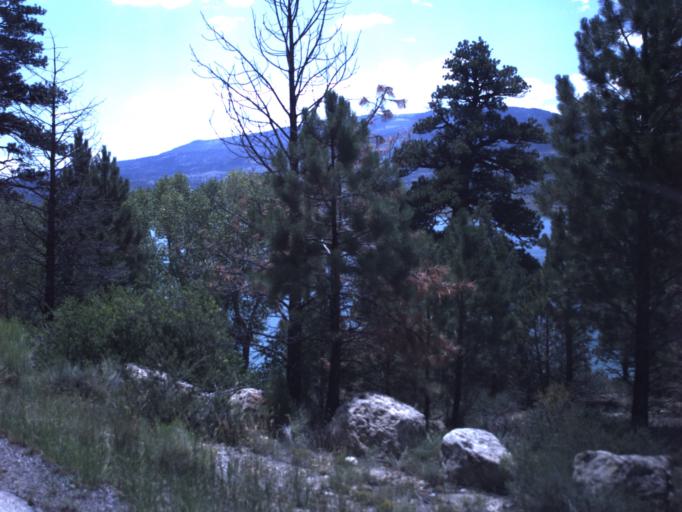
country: US
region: Utah
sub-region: Emery County
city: Orangeville
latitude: 39.3001
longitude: -111.2720
